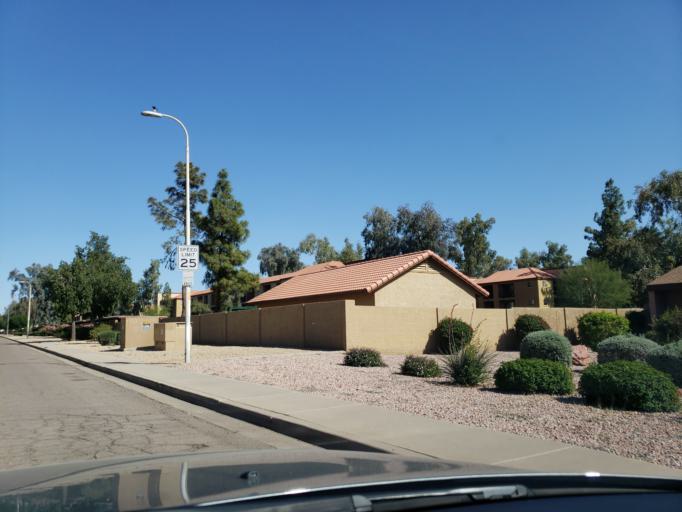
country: US
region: Arizona
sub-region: Maricopa County
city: Glendale
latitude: 33.5565
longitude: -112.1945
